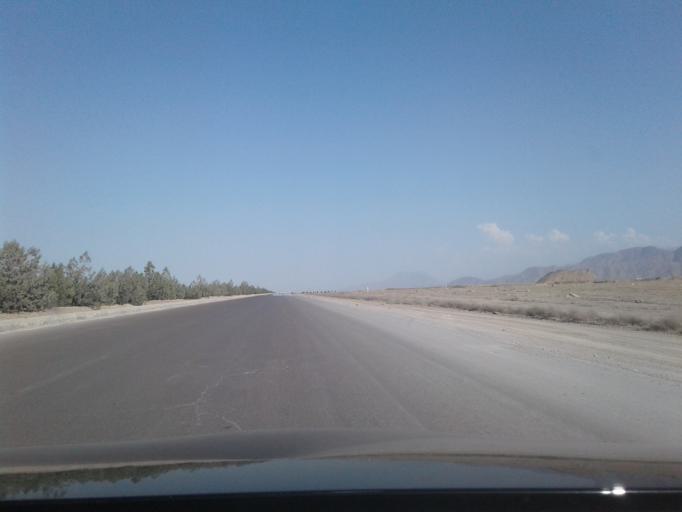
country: TM
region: Ahal
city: Baharly
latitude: 38.2330
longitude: 57.7810
